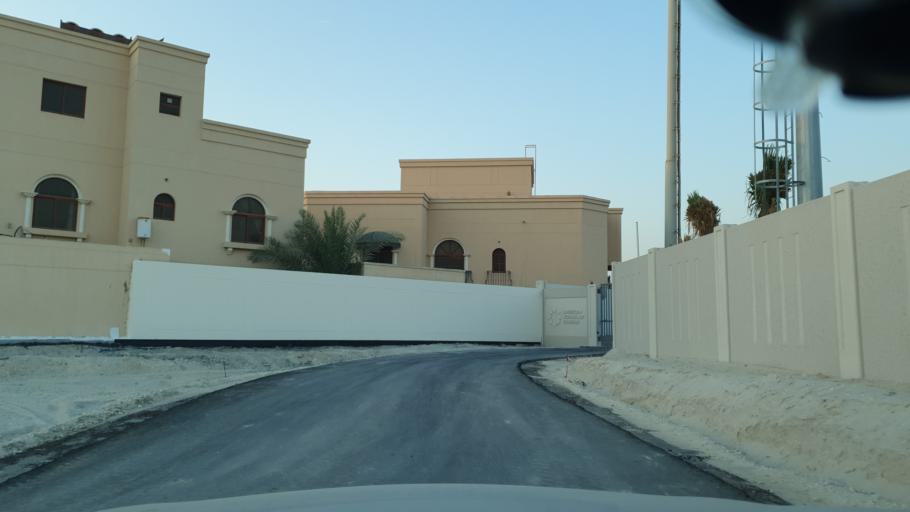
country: BH
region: Northern
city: Madinat `Isa
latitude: 26.1573
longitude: 50.5598
